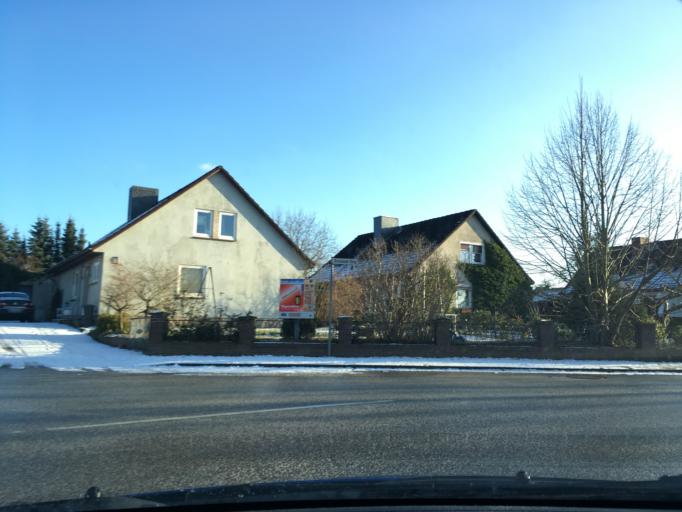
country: DE
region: Schleswig-Holstein
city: Buchen
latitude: 53.4879
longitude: 10.5975
